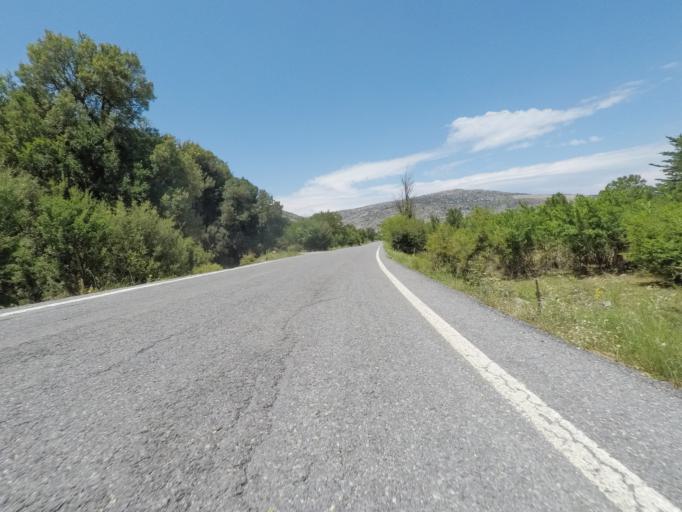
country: GR
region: Crete
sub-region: Nomos Irakleiou
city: Mokhos
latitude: 35.1792
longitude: 25.4341
